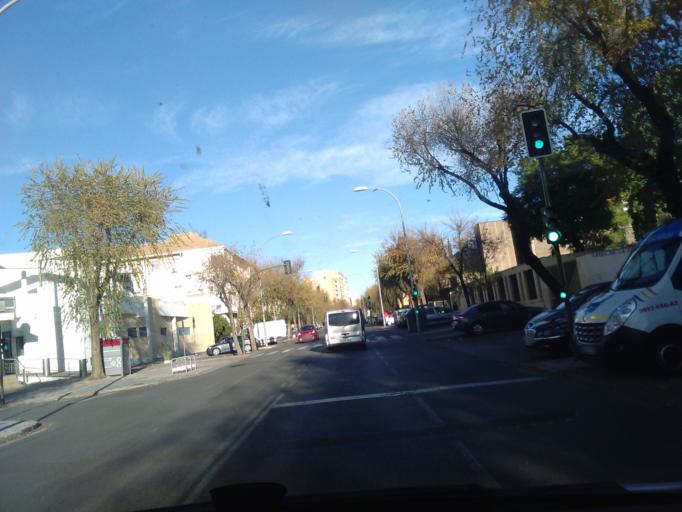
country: ES
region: Andalusia
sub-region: Provincia de Sevilla
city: Sevilla
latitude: 37.3790
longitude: -5.9565
